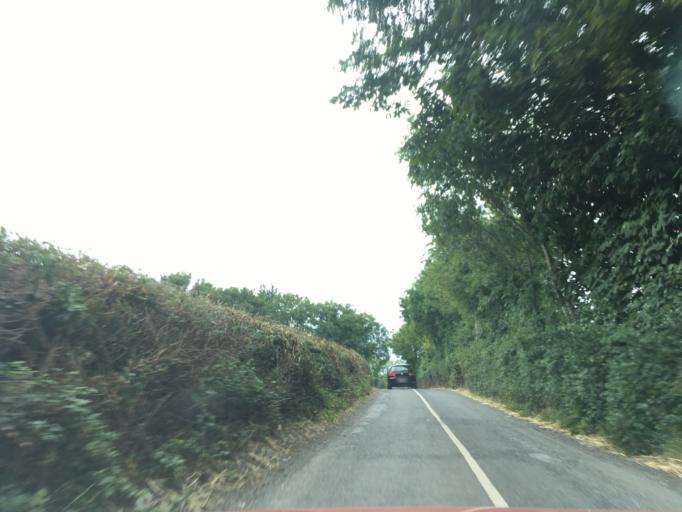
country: IE
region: Munster
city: Cahir
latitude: 52.4601
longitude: -7.9919
